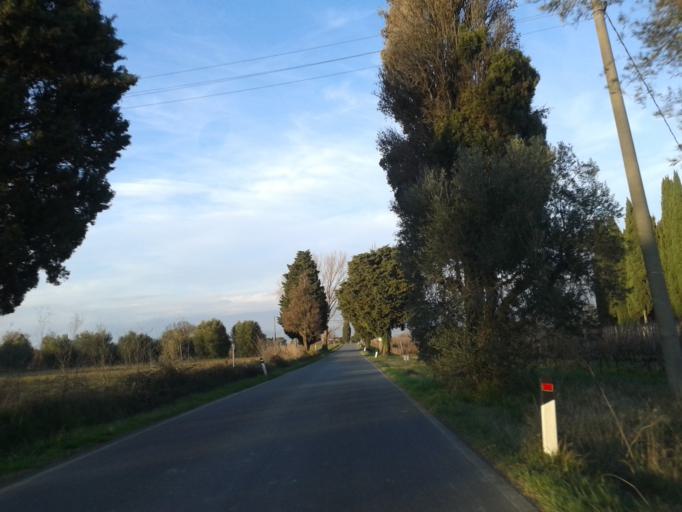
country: IT
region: Tuscany
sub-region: Provincia di Livorno
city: Collesalvetti
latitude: 43.5893
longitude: 10.4454
